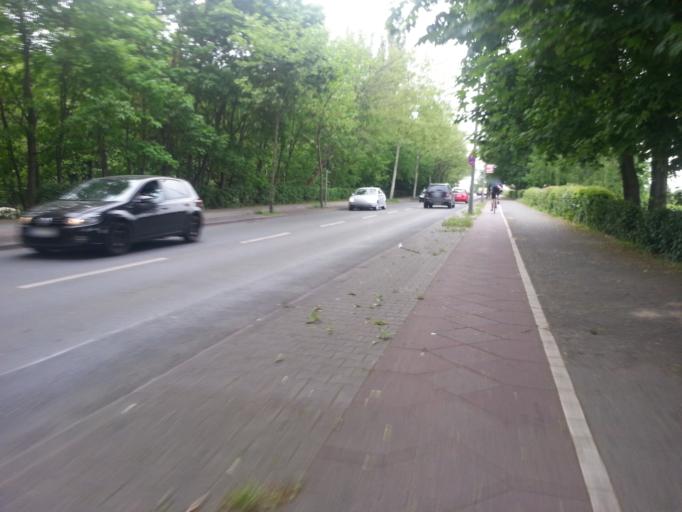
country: DE
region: Berlin
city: Westend
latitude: 52.5269
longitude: 13.2773
